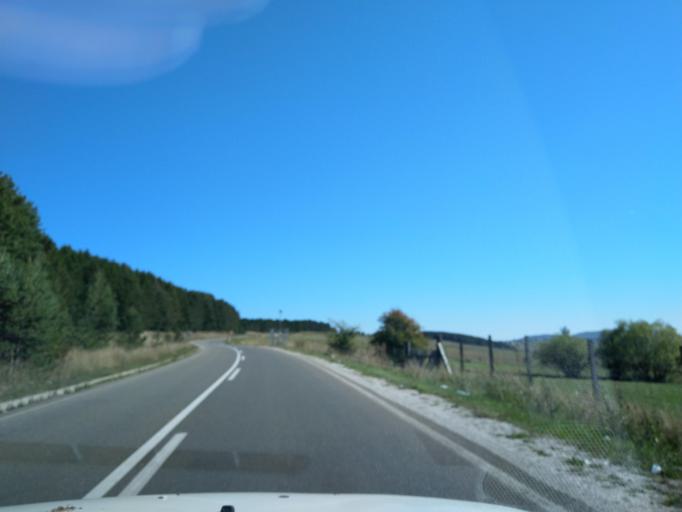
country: RS
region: Central Serbia
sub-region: Zlatiborski Okrug
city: Sjenica
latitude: 43.2682
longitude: 20.0290
